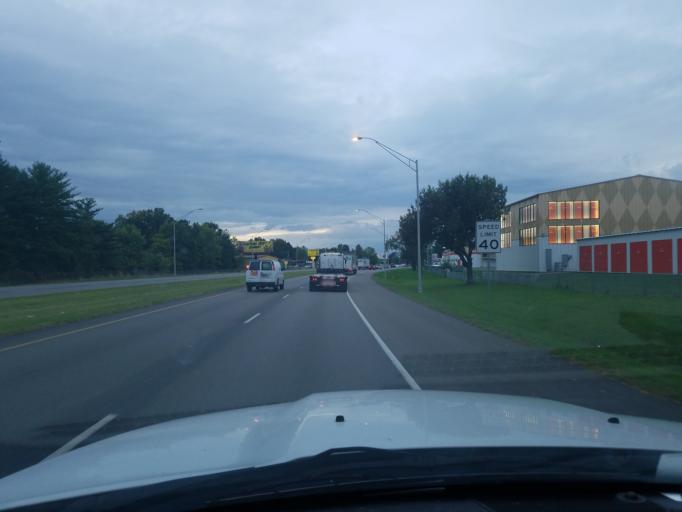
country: US
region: Indiana
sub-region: Vanderburgh County
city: Evansville
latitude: 37.9539
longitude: -87.5422
